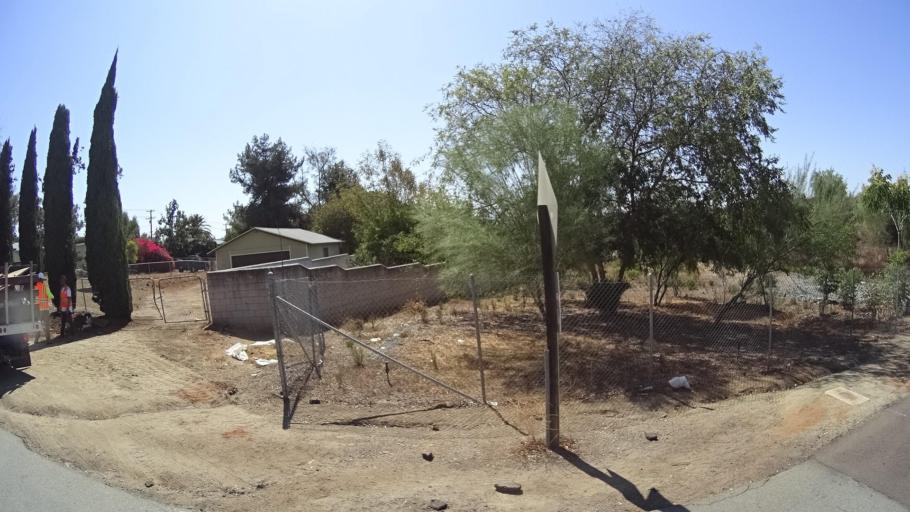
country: US
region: California
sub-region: San Diego County
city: Granite Hills
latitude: 32.8077
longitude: -116.9191
